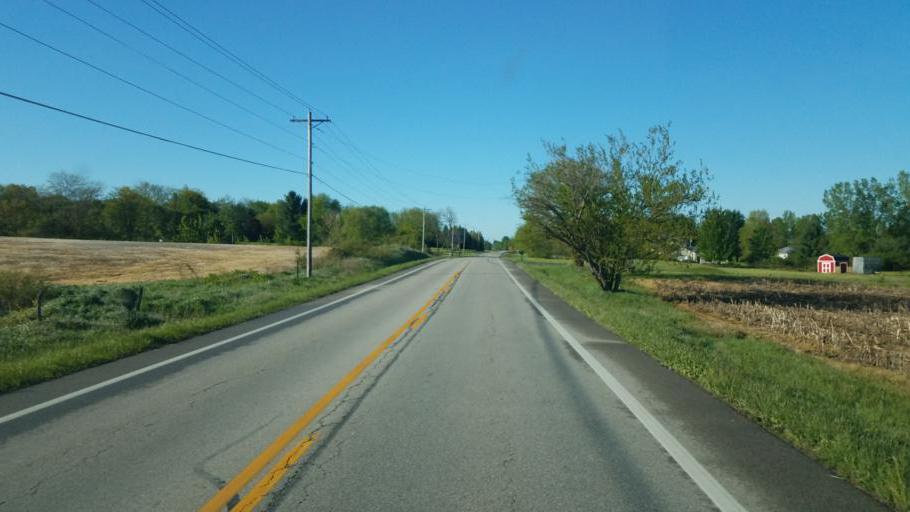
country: US
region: Ohio
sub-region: Delaware County
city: Sunbury
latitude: 40.3074
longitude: -82.8472
